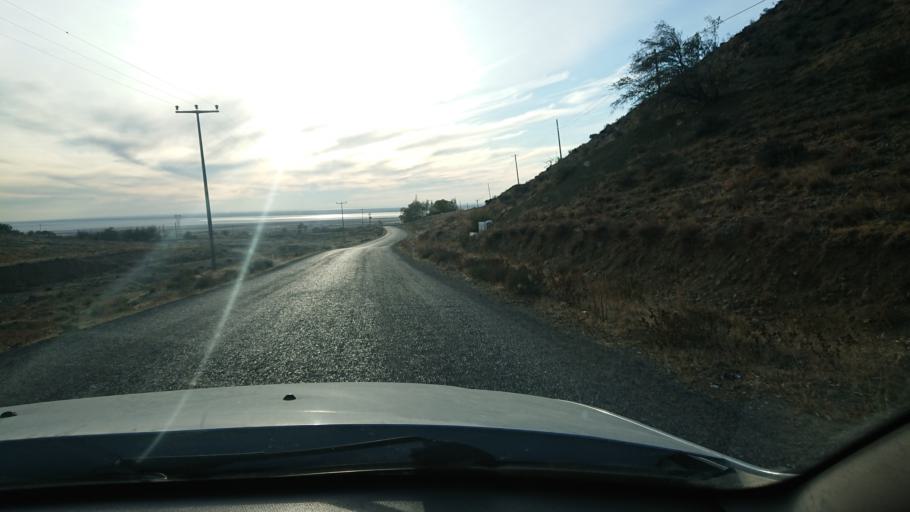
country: TR
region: Ankara
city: Sereflikochisar
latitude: 38.7468
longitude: 33.6838
